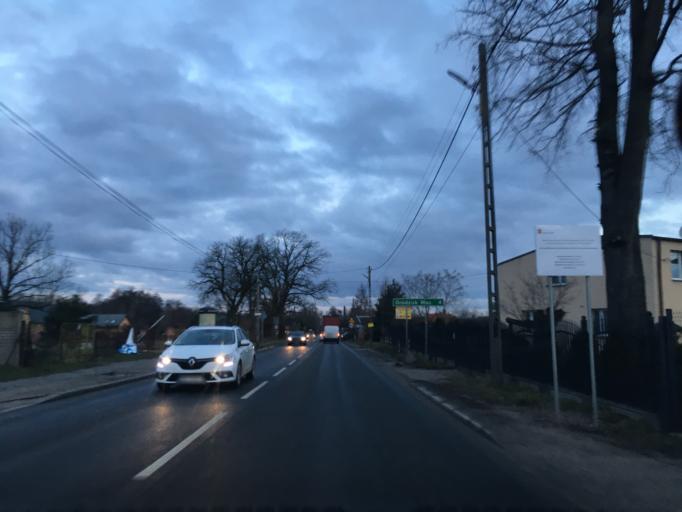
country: PL
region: Masovian Voivodeship
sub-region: Powiat pruszkowski
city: Owczarnia
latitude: 52.0741
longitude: 20.7014
